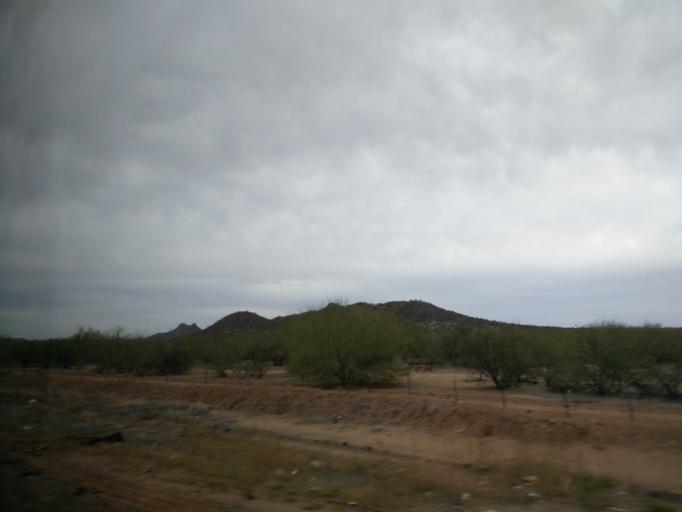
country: MX
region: Sonora
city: Hermosillo
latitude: 28.8439
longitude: -110.9582
